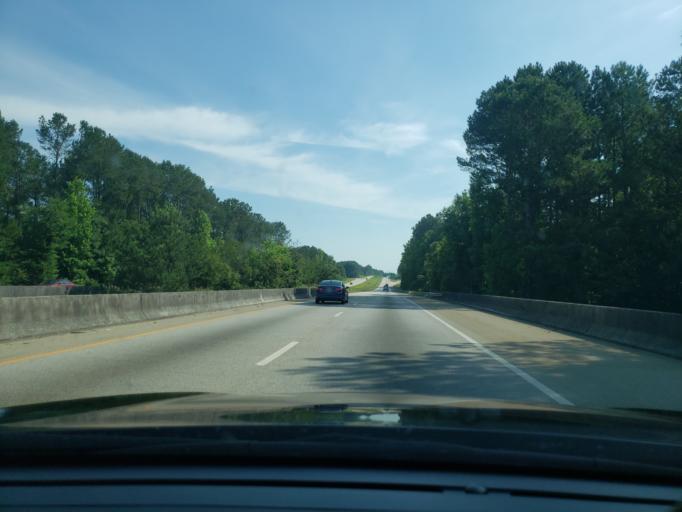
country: US
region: Georgia
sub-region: Troup County
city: La Grange
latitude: 33.0330
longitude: -84.9766
